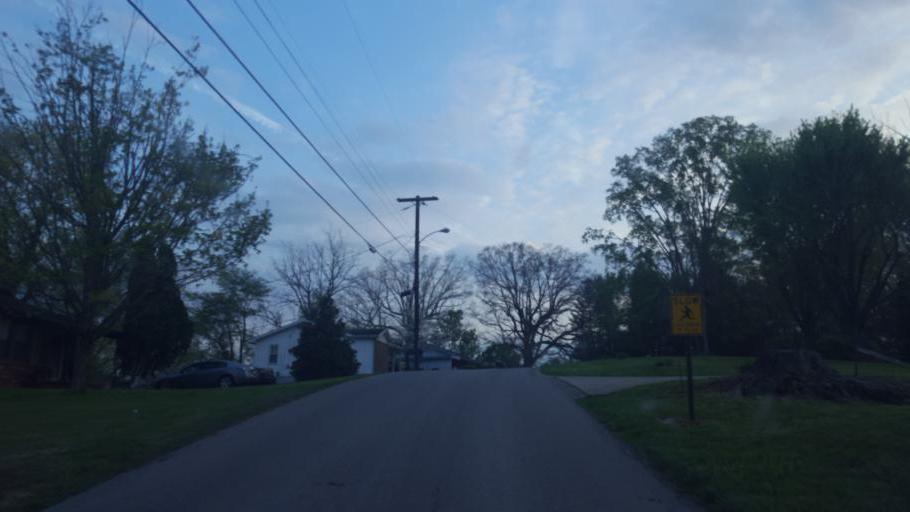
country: US
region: Kentucky
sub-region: Hart County
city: Munfordville
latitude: 37.2758
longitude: -85.9025
